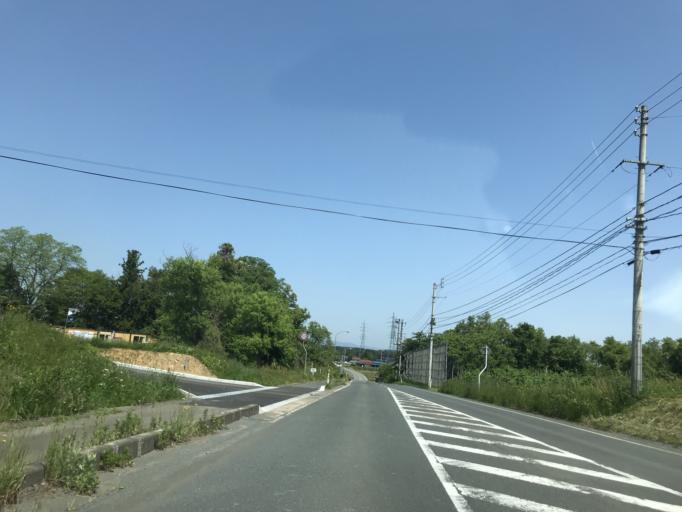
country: JP
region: Iwate
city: Mizusawa
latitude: 39.1737
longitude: 141.0824
